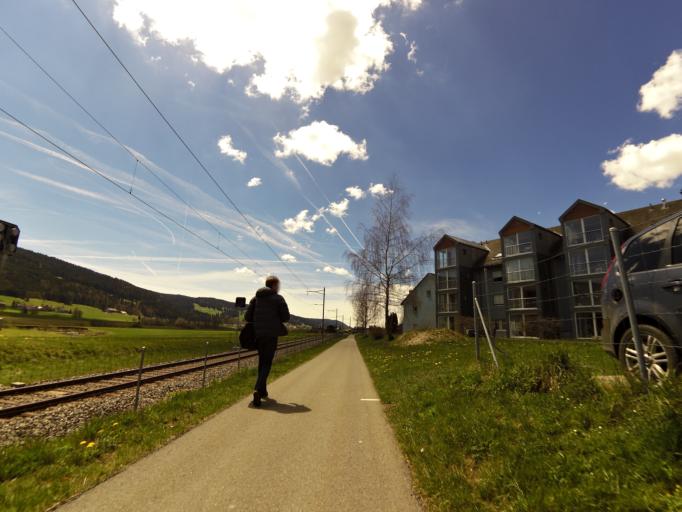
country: CH
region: Vaud
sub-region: Jura-Nord vaudois District
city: Le Chenit
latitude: 46.6007
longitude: 6.2237
